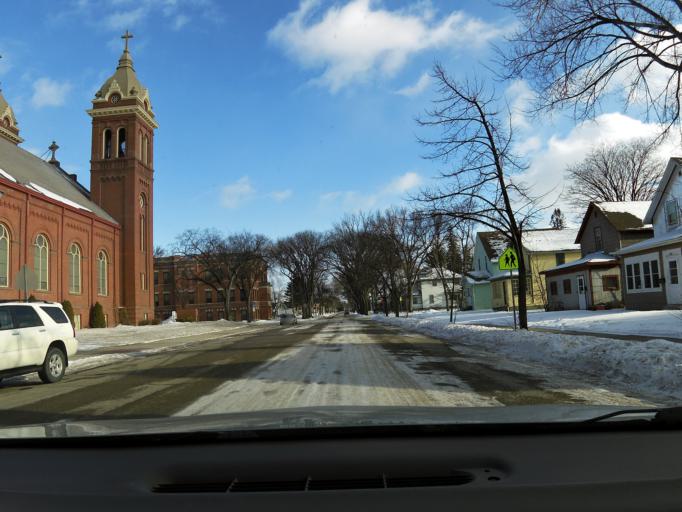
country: US
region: North Dakota
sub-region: Grand Forks County
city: Grand Forks
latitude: 47.9267
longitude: -97.0403
